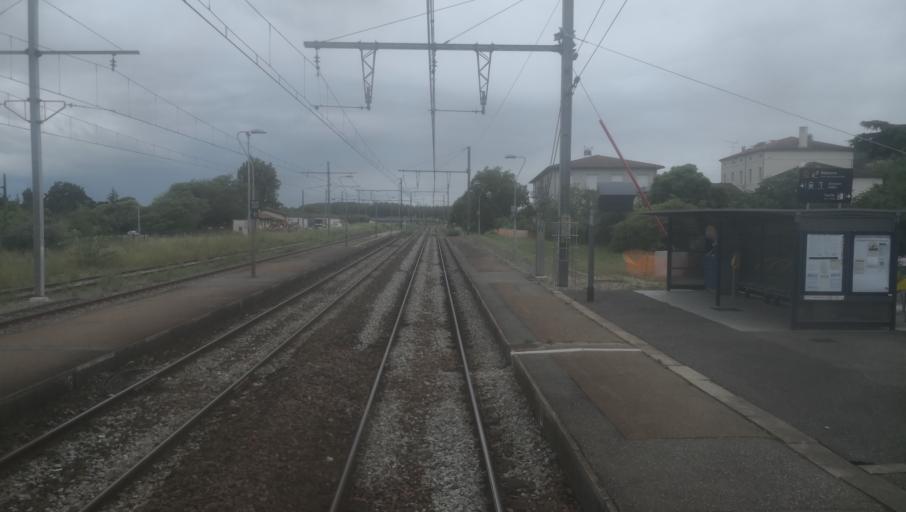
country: FR
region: Aquitaine
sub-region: Departement du Lot-et-Garonne
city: Port-Sainte-Marie
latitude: 44.2507
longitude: 0.3895
